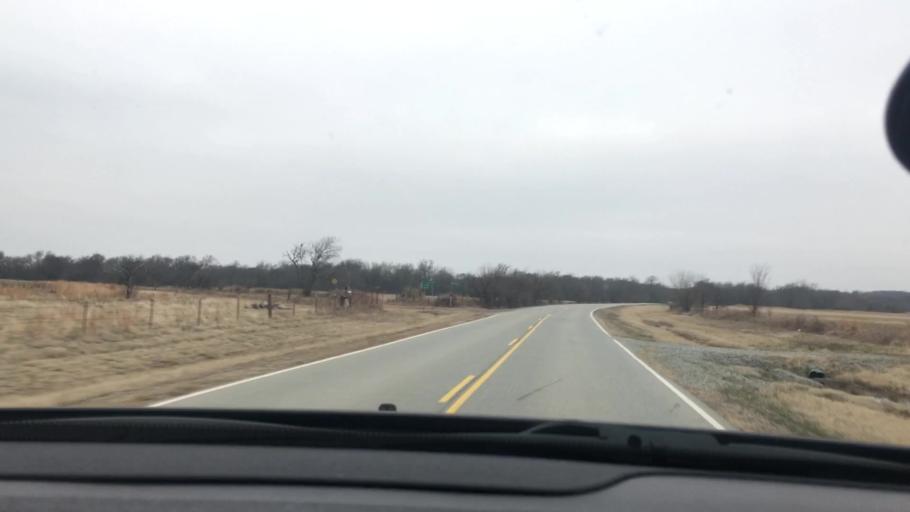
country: US
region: Oklahoma
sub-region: Coal County
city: Coalgate
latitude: 34.5321
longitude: -96.2541
